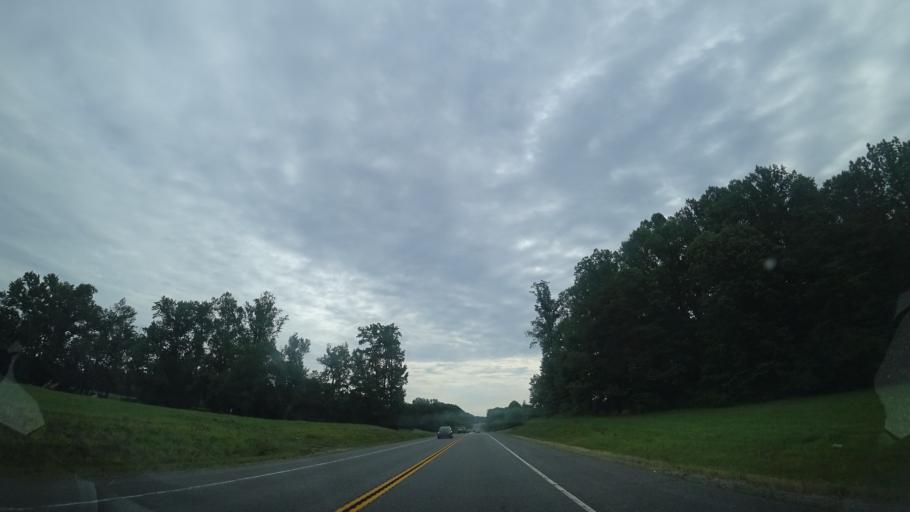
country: US
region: Virginia
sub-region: Spotsylvania County
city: Spotsylvania Courthouse
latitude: 38.1607
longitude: -77.6661
